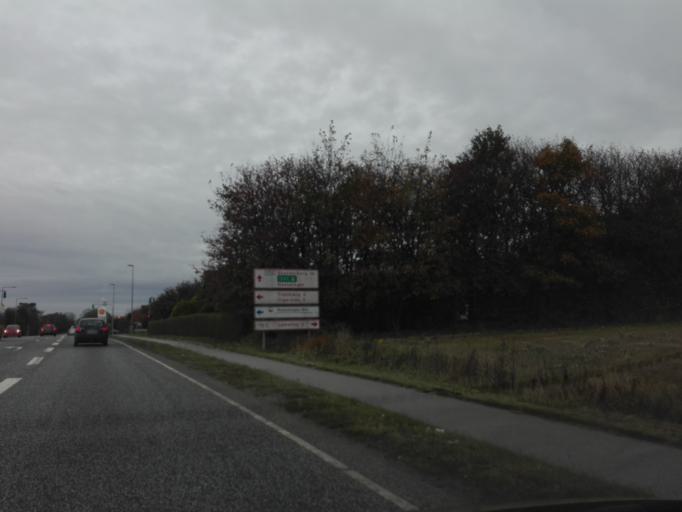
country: DK
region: Central Jutland
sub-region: Arhus Kommune
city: Tranbjerg
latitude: 56.1078
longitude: 10.1126
